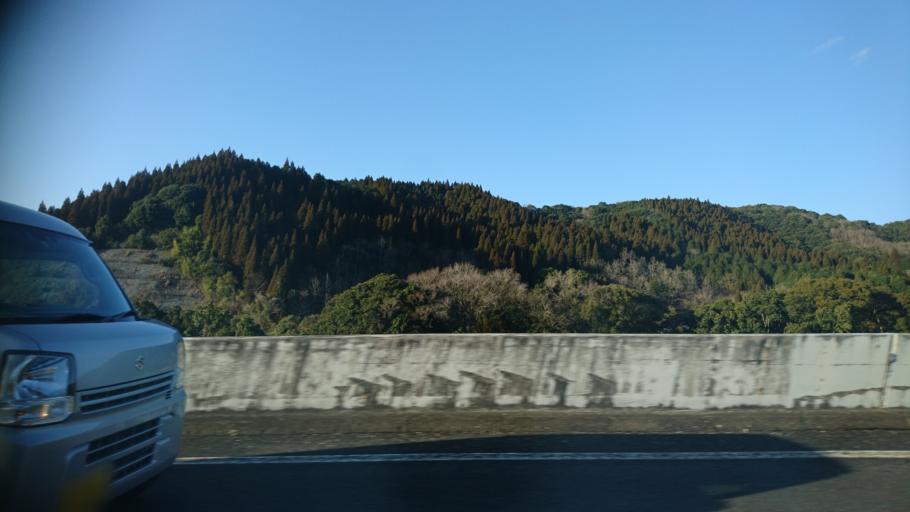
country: JP
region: Miyazaki
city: Miyakonojo
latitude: 31.7918
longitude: 131.1834
